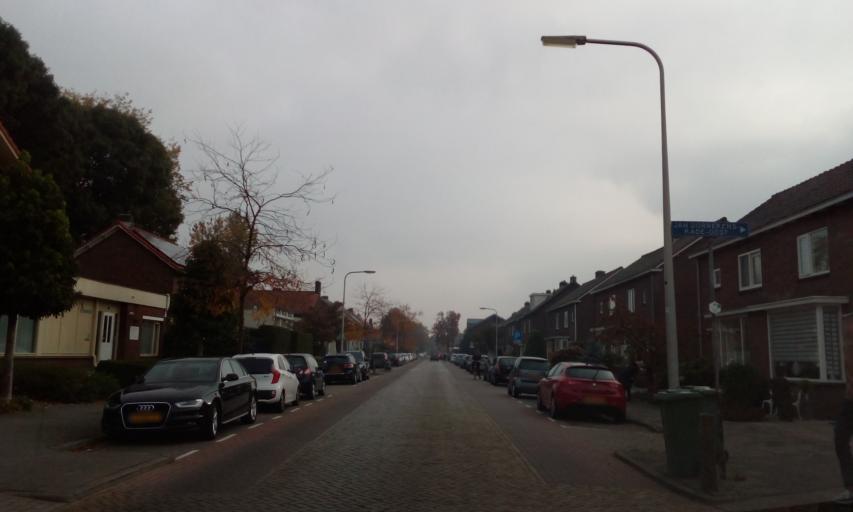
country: NL
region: South Holland
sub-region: Gemeente Waddinxveen
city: Waddinxveen
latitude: 52.0444
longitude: 4.6510
